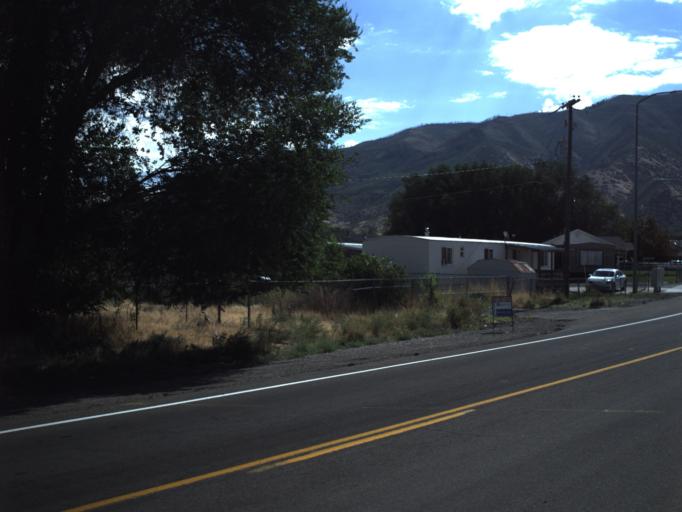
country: US
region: Utah
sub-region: Utah County
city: Santaquin
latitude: 39.9762
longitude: -111.7953
